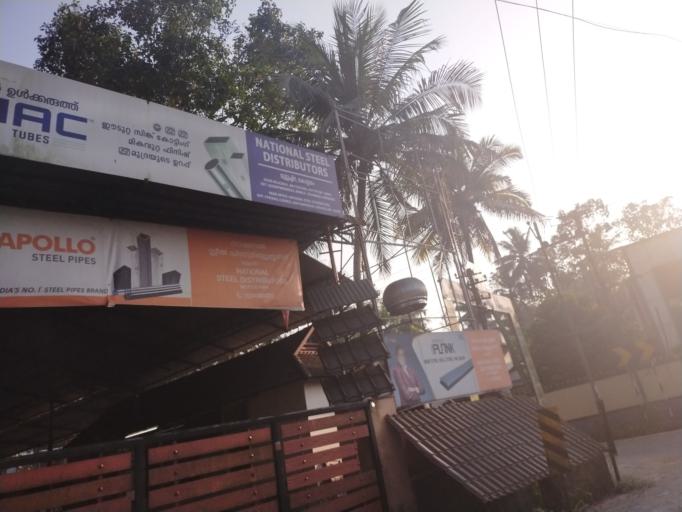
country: IN
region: Kerala
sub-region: Kottayam
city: Vaikam
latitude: 9.7541
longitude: 76.5017
